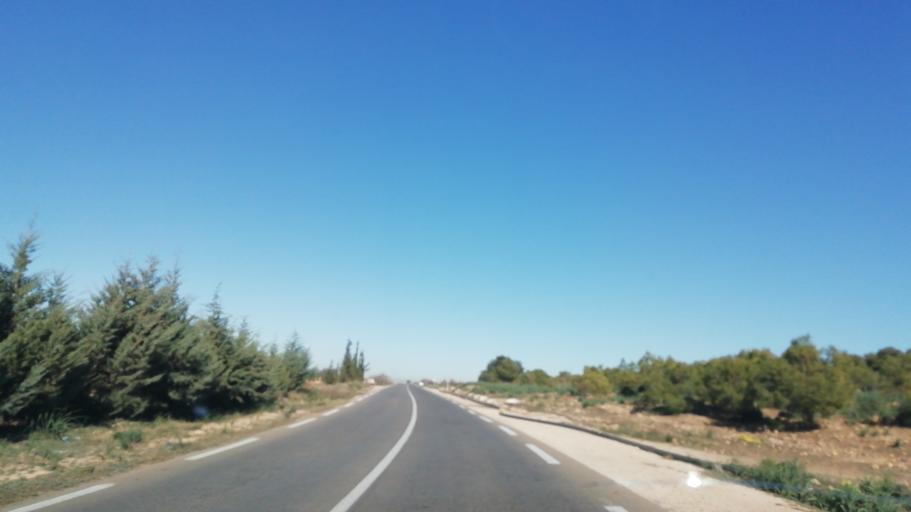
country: DZ
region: Tlemcen
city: Beni Mester
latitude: 34.8174
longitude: -1.6147
